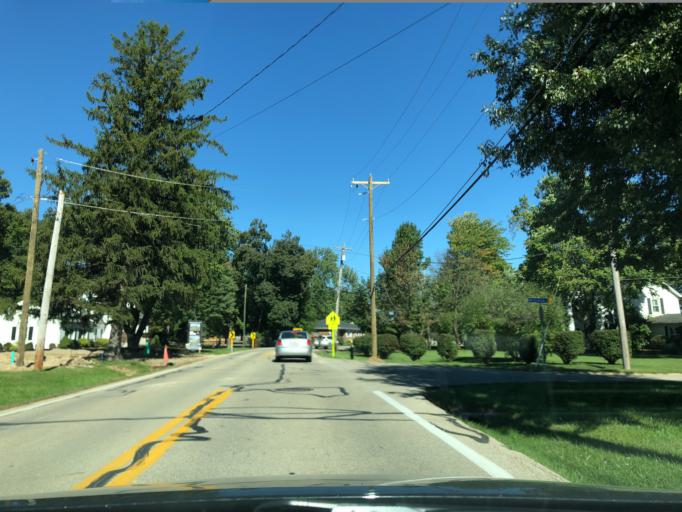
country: US
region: Ohio
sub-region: Hamilton County
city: Sixteen Mile Stand
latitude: 39.2811
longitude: -84.3111
